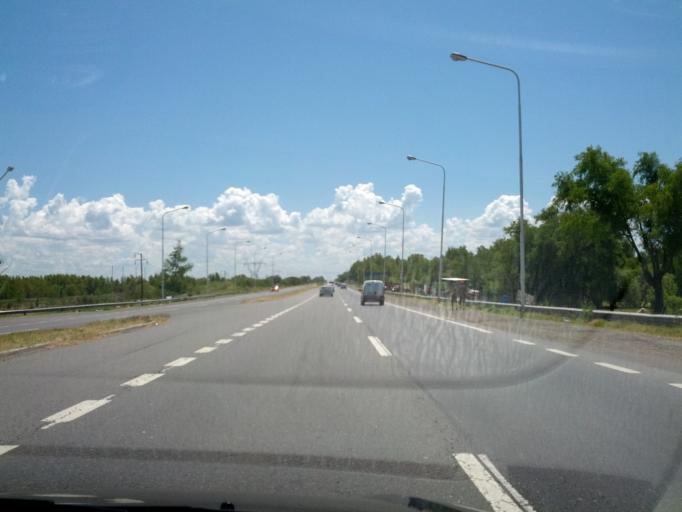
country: AR
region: Entre Rios
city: Villa Paranacito
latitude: -33.7280
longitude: -58.8527
